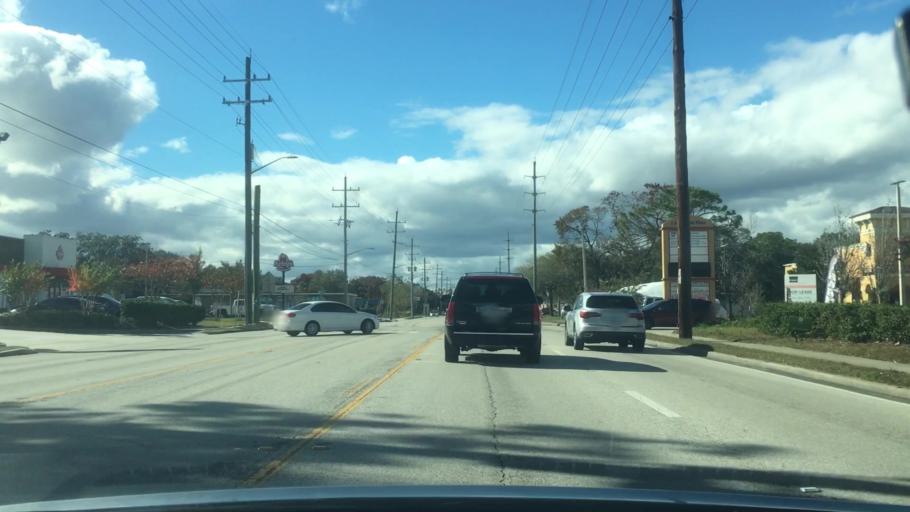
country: US
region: Florida
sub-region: Duval County
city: Jacksonville
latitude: 30.3522
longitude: -81.5698
